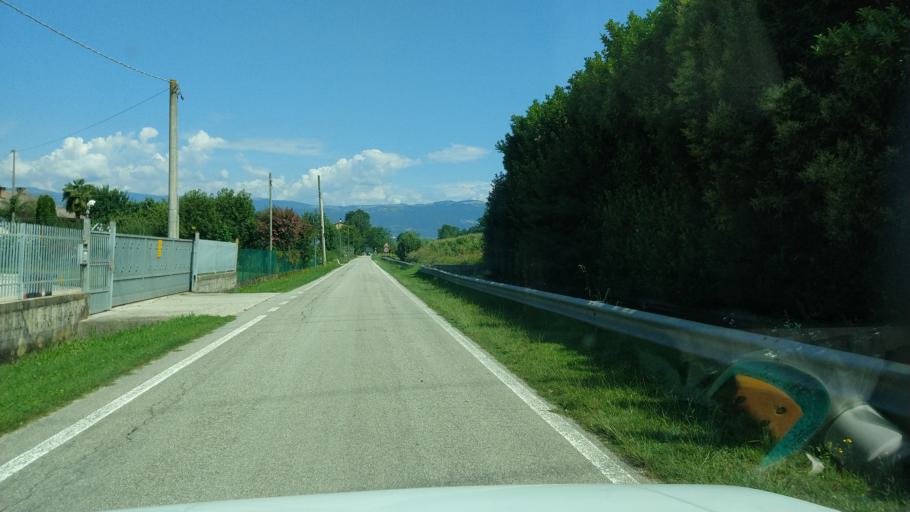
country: IT
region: Veneto
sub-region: Provincia di Vicenza
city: Tezze
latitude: 45.6894
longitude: 11.6797
